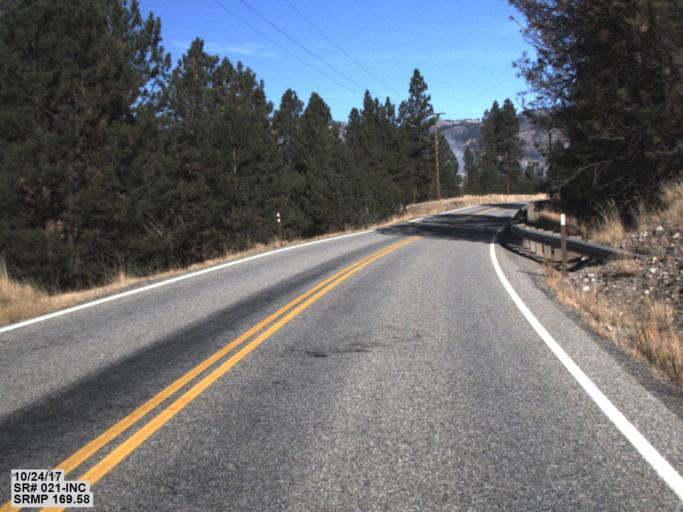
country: US
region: Washington
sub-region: Ferry County
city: Republic
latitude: 48.7373
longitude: -118.6605
